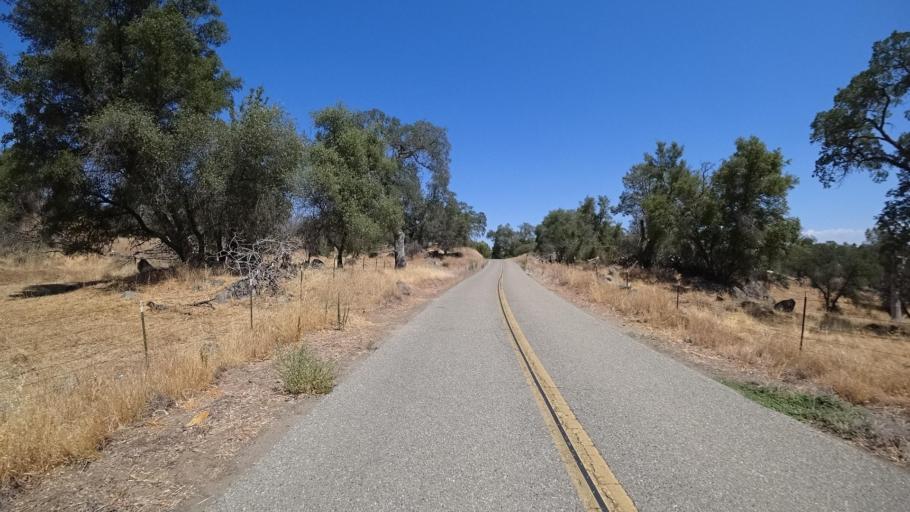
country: US
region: California
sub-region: Mariposa County
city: Mariposa
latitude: 37.3028
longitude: -119.9762
